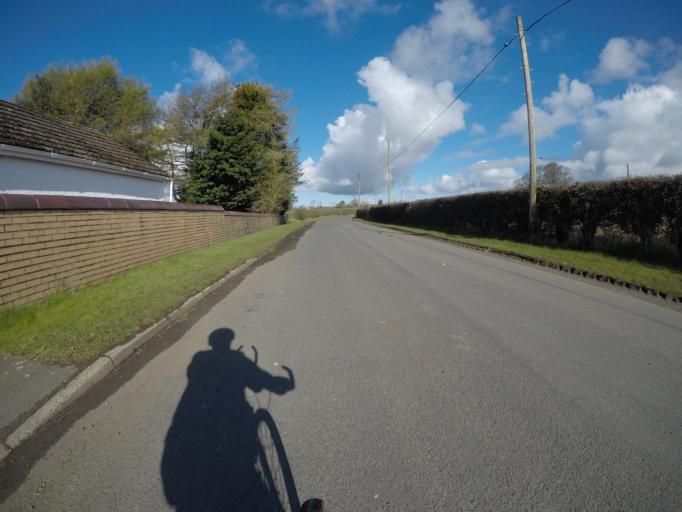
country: GB
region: Scotland
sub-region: North Ayrshire
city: Irvine
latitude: 55.6545
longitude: -4.6524
